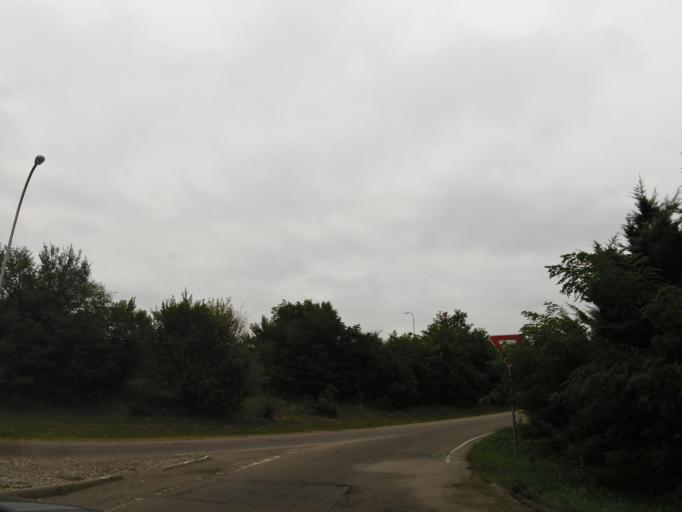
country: US
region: Colorado
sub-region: El Paso County
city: Colorado Springs
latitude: 38.7969
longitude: -104.8232
